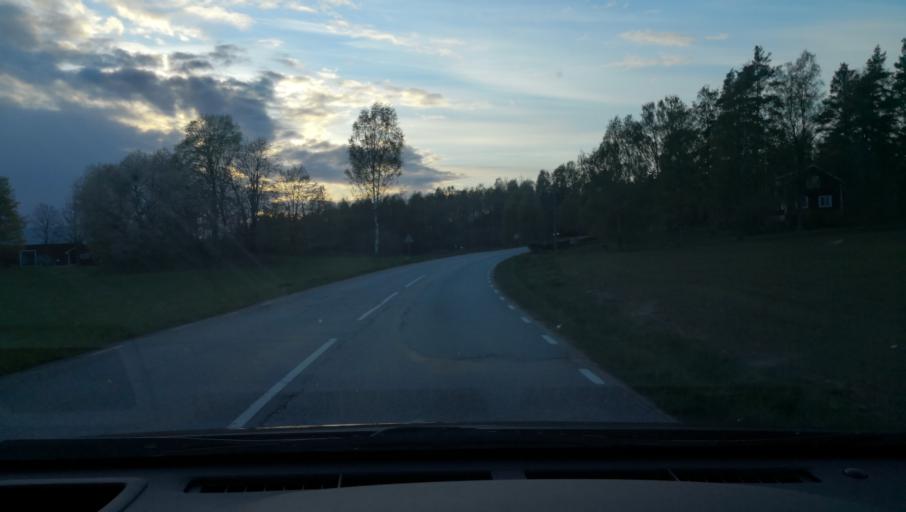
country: SE
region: OErebro
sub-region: Askersunds Kommun
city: Asbro
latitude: 58.9330
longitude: 15.0232
